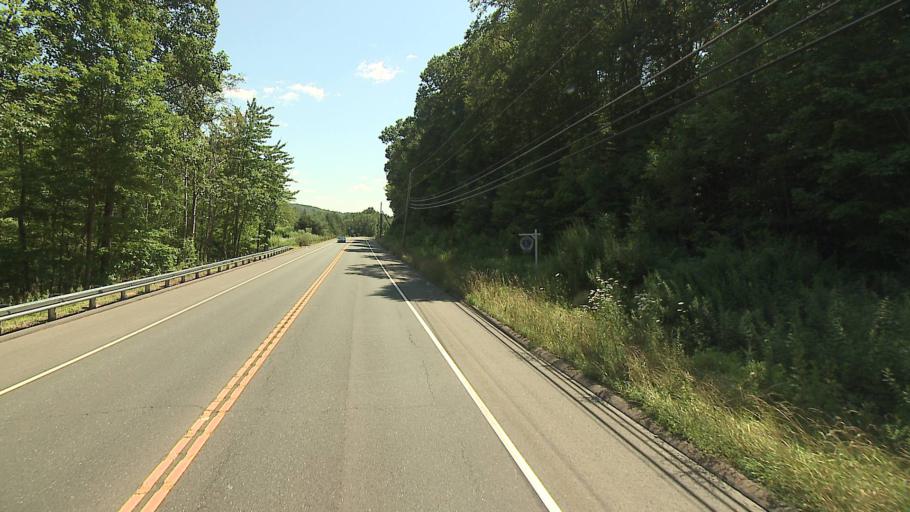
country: US
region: Connecticut
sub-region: Litchfield County
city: Northwest Harwinton
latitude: 41.7871
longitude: -73.0747
